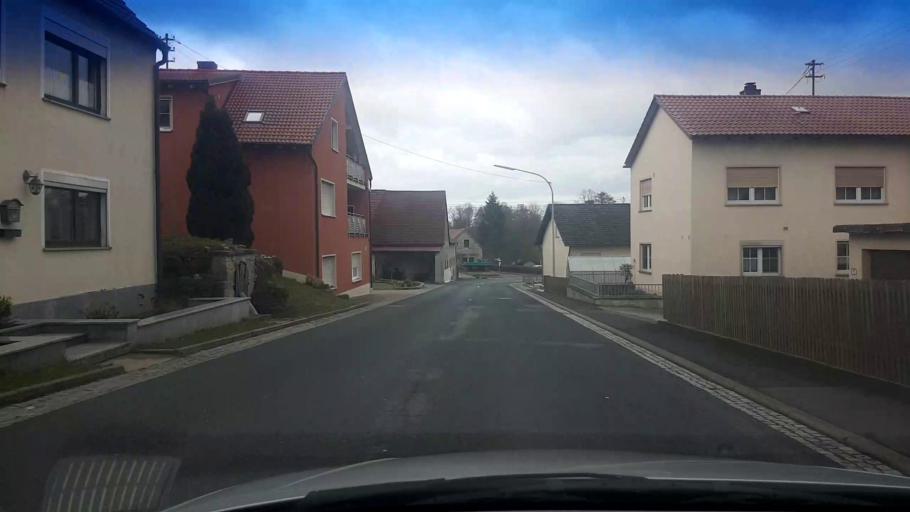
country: DE
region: Bavaria
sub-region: Regierungsbezirk Unterfranken
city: Eltmann
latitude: 49.9315
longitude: 10.6516
